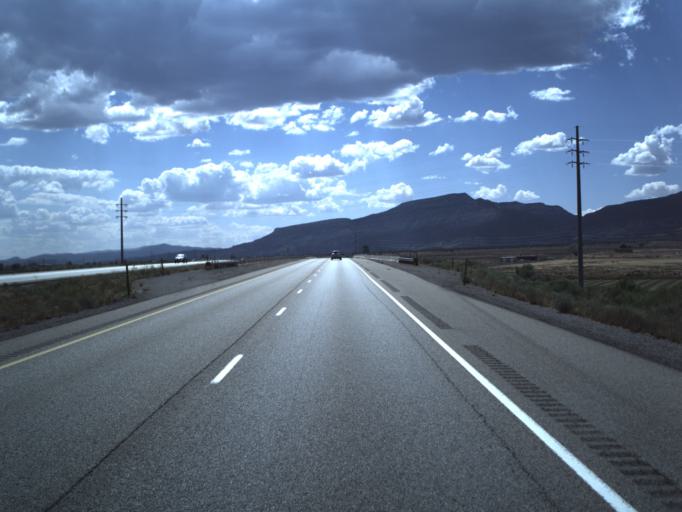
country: US
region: Utah
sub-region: Sevier County
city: Aurora
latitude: 38.8777
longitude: -111.9552
